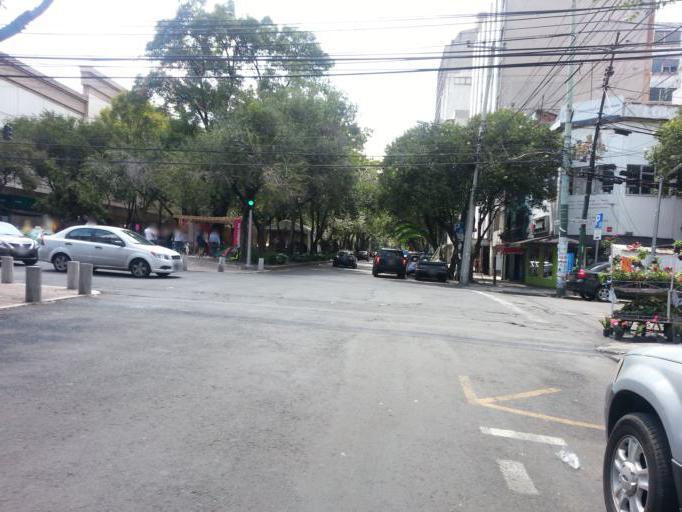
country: MX
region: Mexico City
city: Benito Juarez
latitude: 19.4197
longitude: -99.1679
